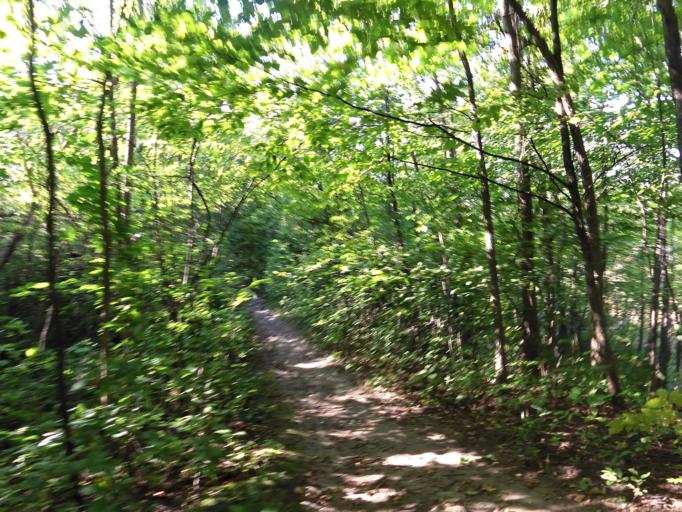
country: CA
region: Ontario
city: Ottawa
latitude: 45.4281
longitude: -75.7421
